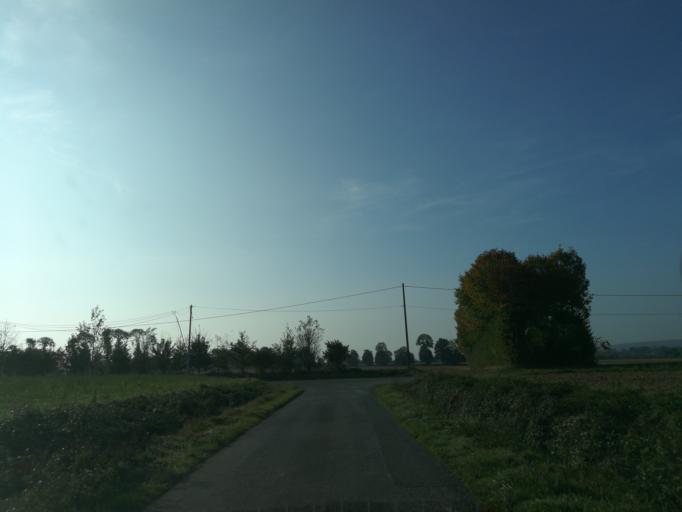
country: FR
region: Brittany
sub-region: Departement d'Ille-et-Vilaine
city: Breteil
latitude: 48.1562
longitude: -1.9078
